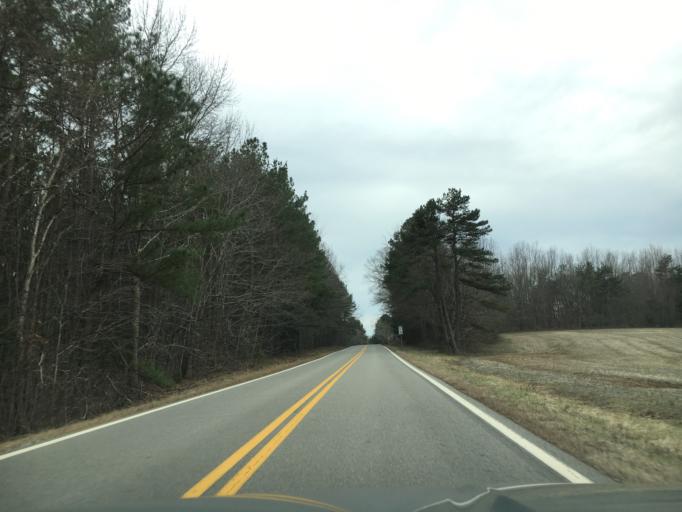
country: US
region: Virginia
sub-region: Charlotte County
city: Charlotte Court House
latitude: 36.9824
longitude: -78.6971
